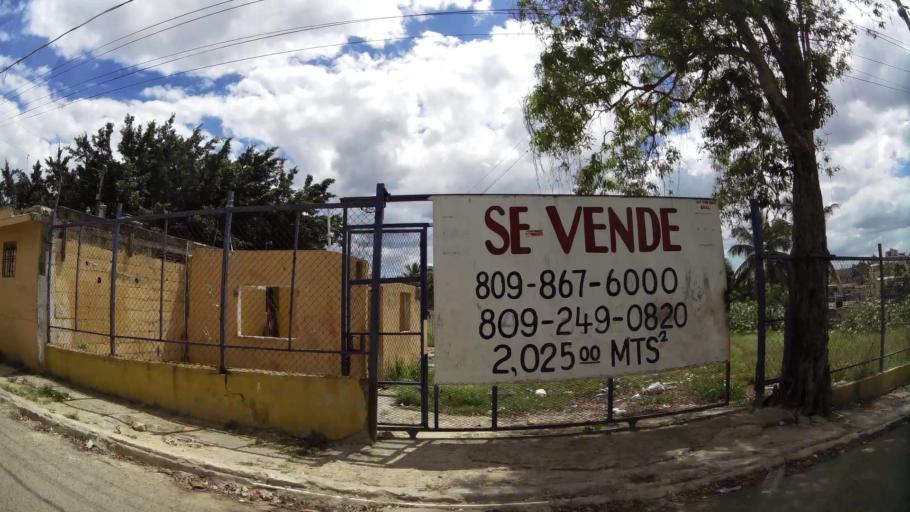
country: DO
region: Nacional
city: Ensanche Luperon
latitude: 18.5246
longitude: -69.9142
